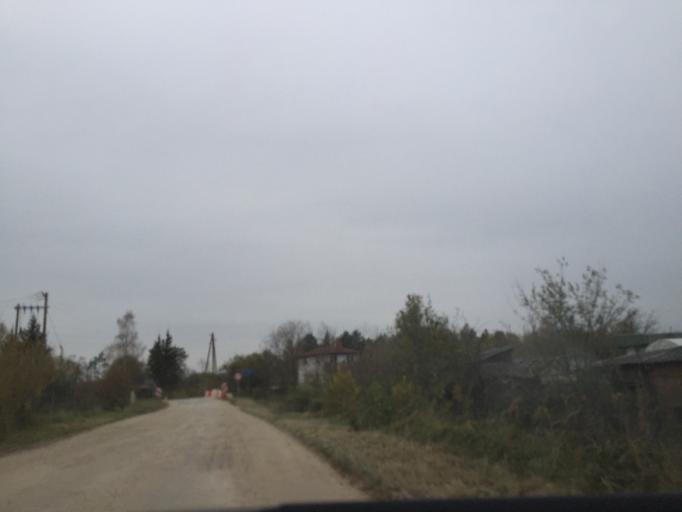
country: LV
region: Jelgava
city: Jelgava
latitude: 56.6354
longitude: 23.6223
